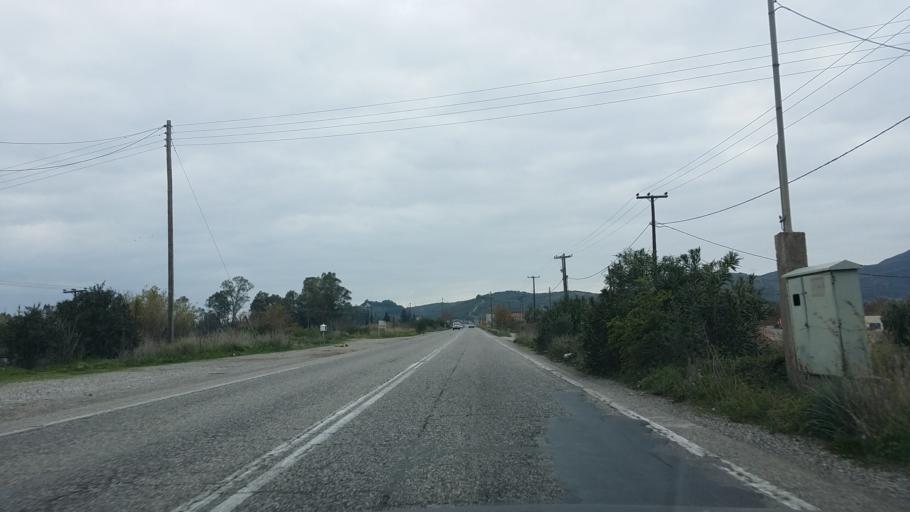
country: GR
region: West Greece
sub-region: Nomos Aitolias kai Akarnanias
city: Galatas
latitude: 38.3773
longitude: 21.5576
